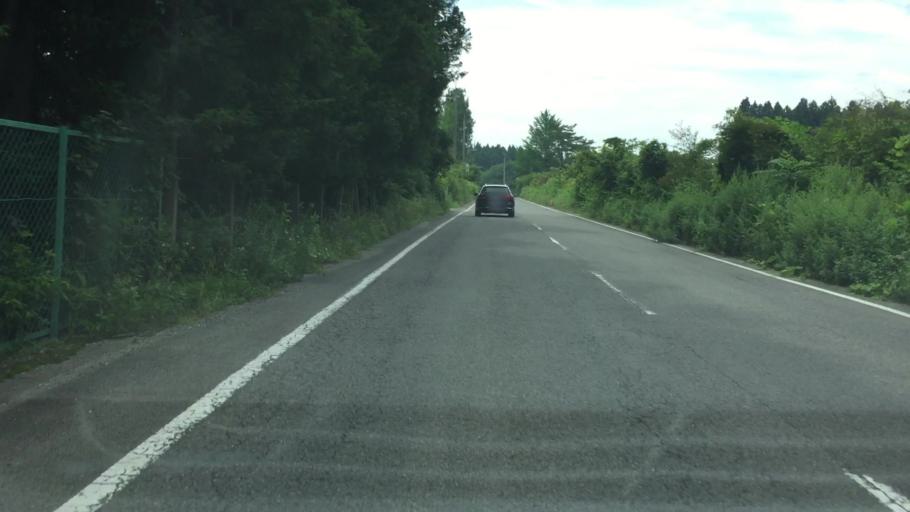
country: JP
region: Tochigi
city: Kuroiso
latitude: 37.0449
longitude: 140.0429
